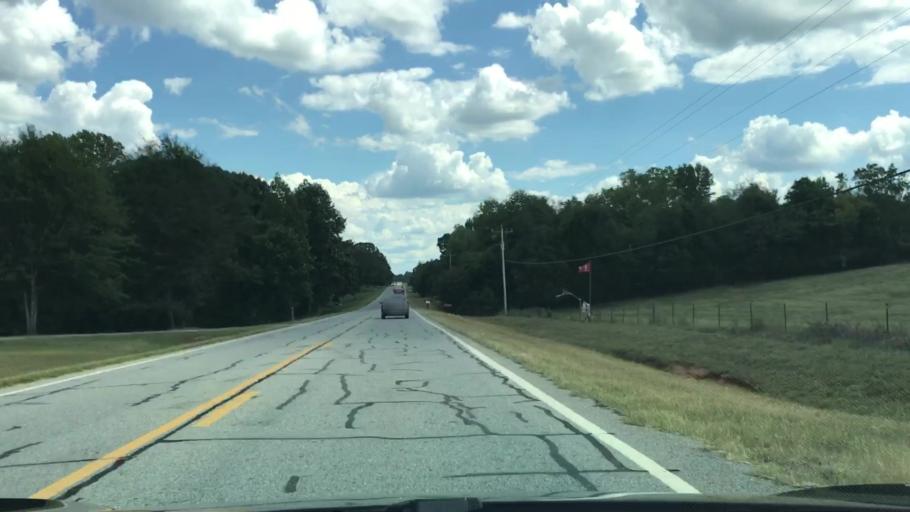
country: US
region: Georgia
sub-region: Oconee County
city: Watkinsville
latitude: 33.8021
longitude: -83.3399
